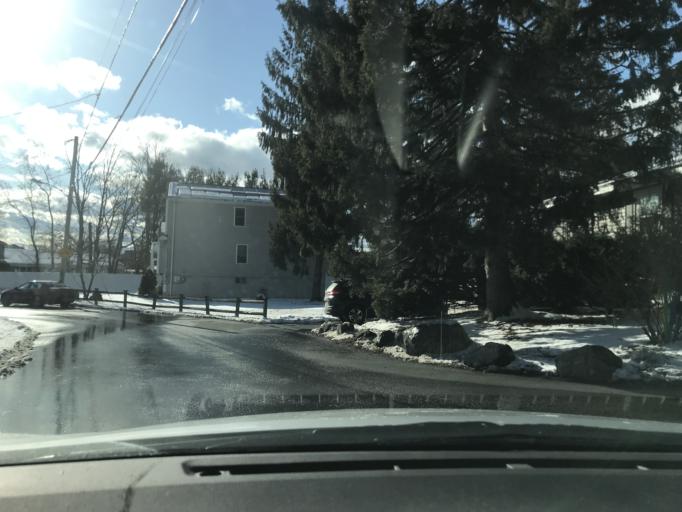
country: US
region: Massachusetts
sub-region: Essex County
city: Saugus
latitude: 42.4908
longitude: -71.0139
